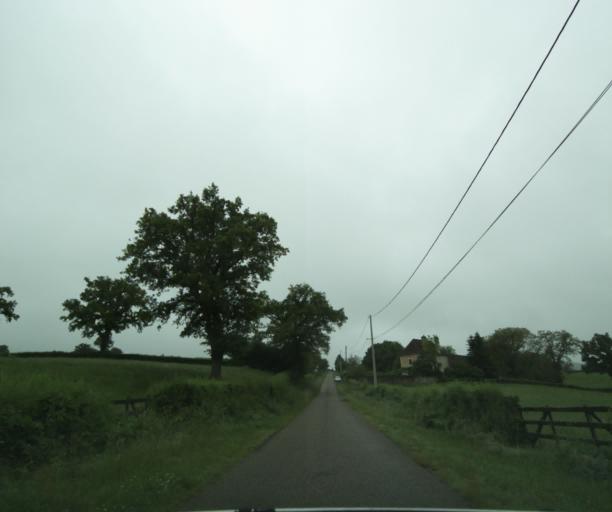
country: FR
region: Bourgogne
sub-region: Departement de Saone-et-Loire
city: Charolles
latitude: 46.4338
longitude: 4.4139
